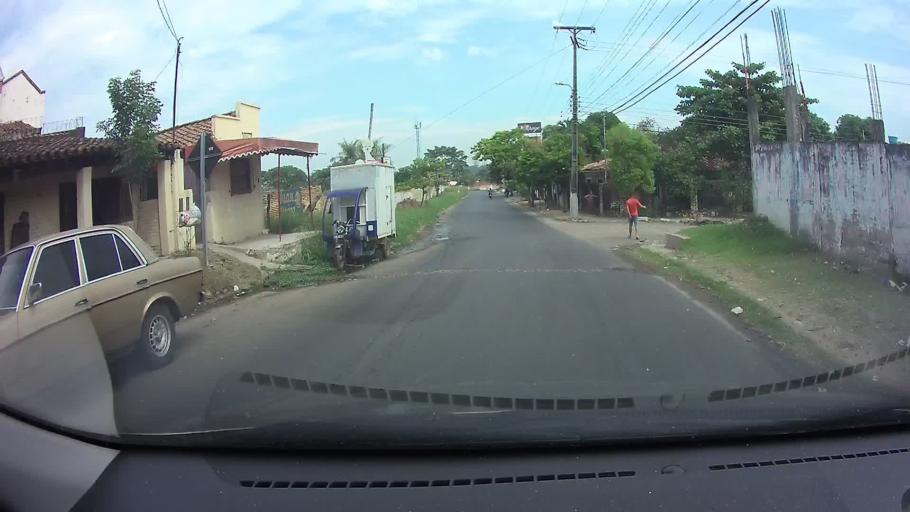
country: PY
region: Central
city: Fernando de la Mora
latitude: -25.3043
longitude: -57.5421
